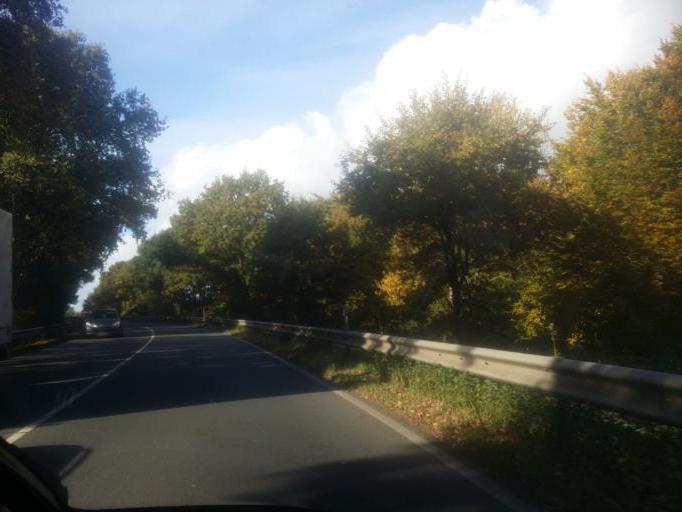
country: DE
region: Schleswig-Holstein
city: Elmshorn
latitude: 53.7744
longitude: 9.6695
